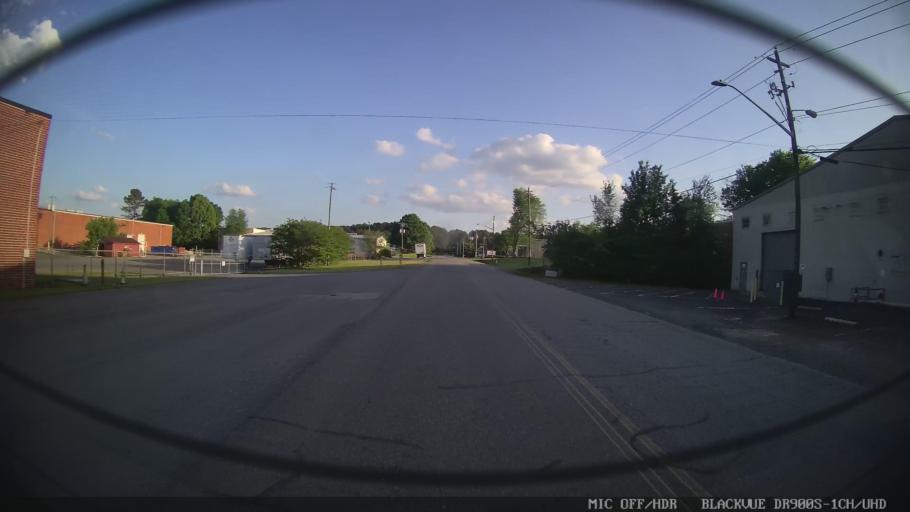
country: US
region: Georgia
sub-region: Bartow County
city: Cartersville
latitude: 34.1486
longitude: -84.7971
